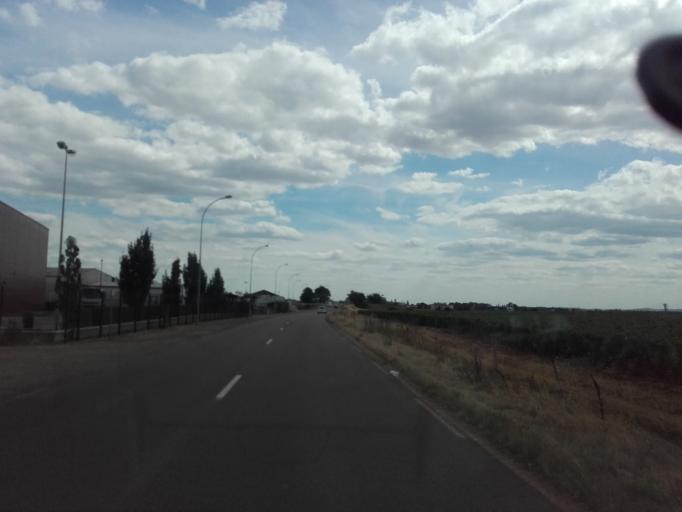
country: FR
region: Bourgogne
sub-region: Departement de la Cote-d'Or
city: Beaune
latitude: 47.0496
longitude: 4.8394
